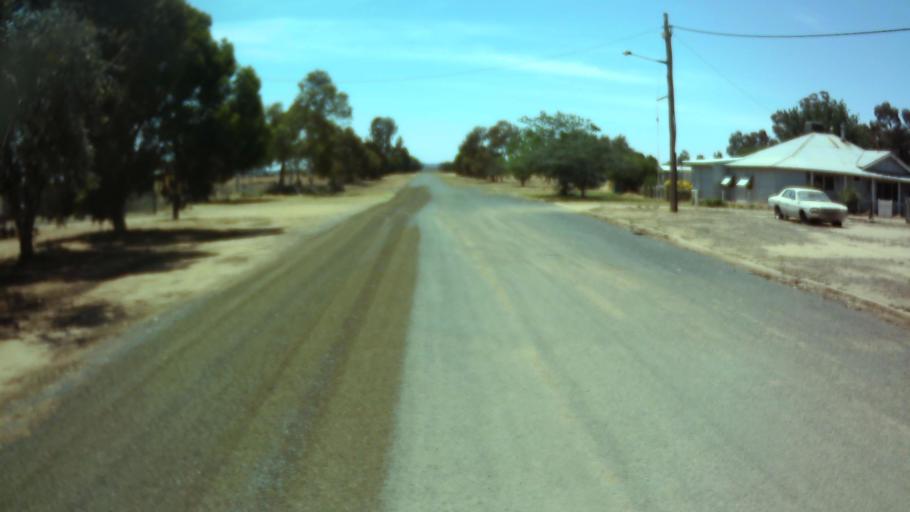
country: AU
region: New South Wales
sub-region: Weddin
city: Grenfell
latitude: -33.8433
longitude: 147.7391
